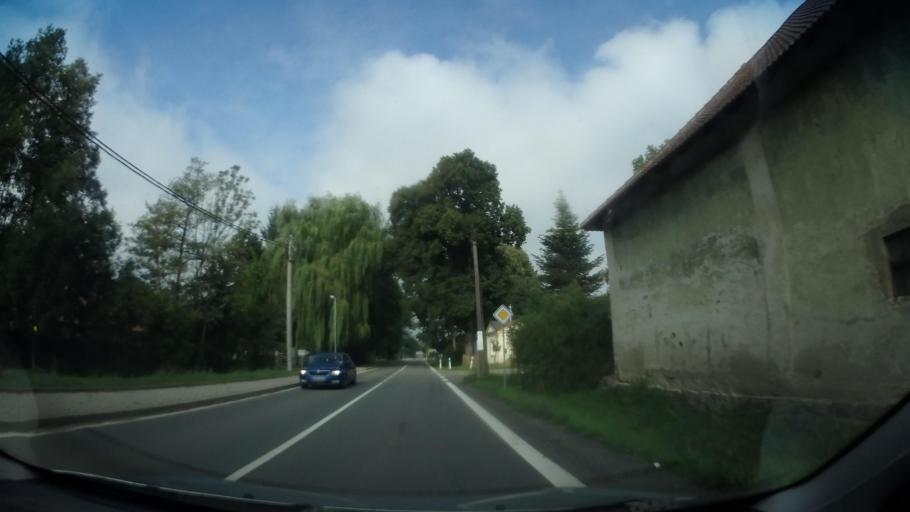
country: CZ
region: Central Bohemia
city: Bystrice
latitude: 49.7564
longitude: 14.6682
